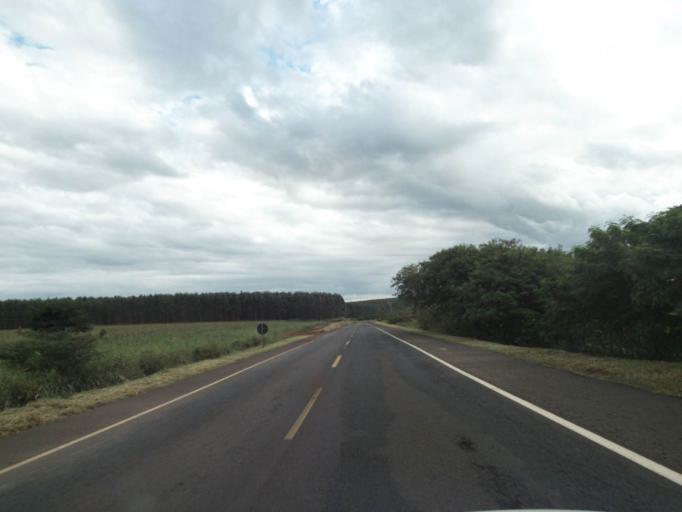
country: PY
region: Canindeyu
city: Salto del Guaira
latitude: -24.0846
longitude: -54.0766
